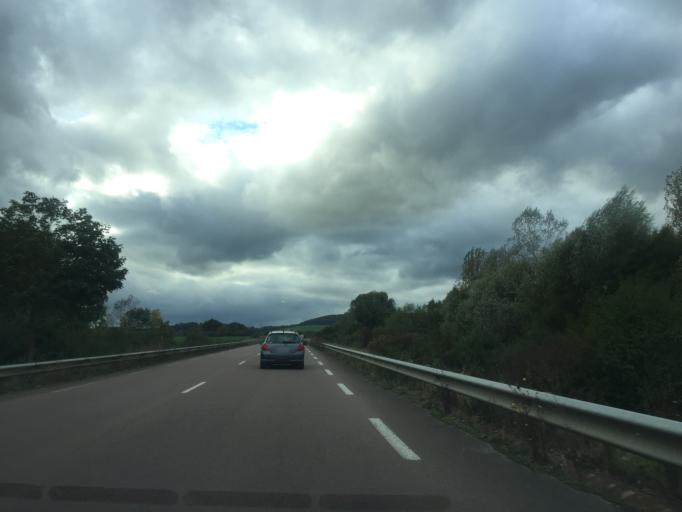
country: FR
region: Lorraine
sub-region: Departement des Vosges
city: Chatenois
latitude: 48.2961
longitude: 5.8591
